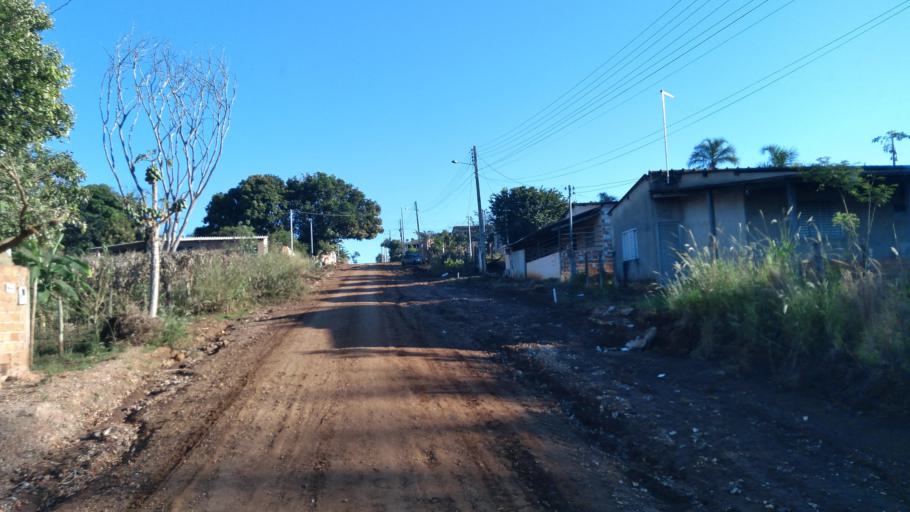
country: BR
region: Goias
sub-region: Mineiros
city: Mineiros
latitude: -17.5885
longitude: -52.5490
